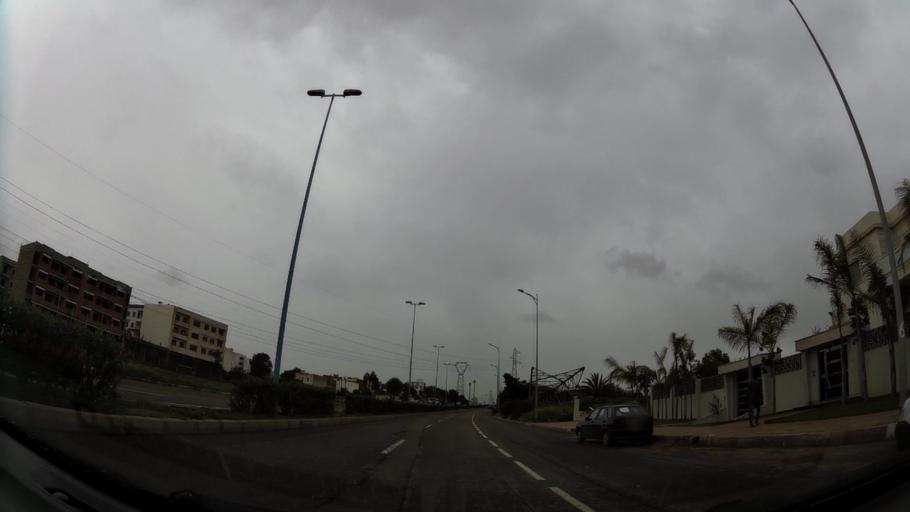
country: MA
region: Grand Casablanca
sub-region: Casablanca
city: Casablanca
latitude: 33.5385
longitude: -7.6178
